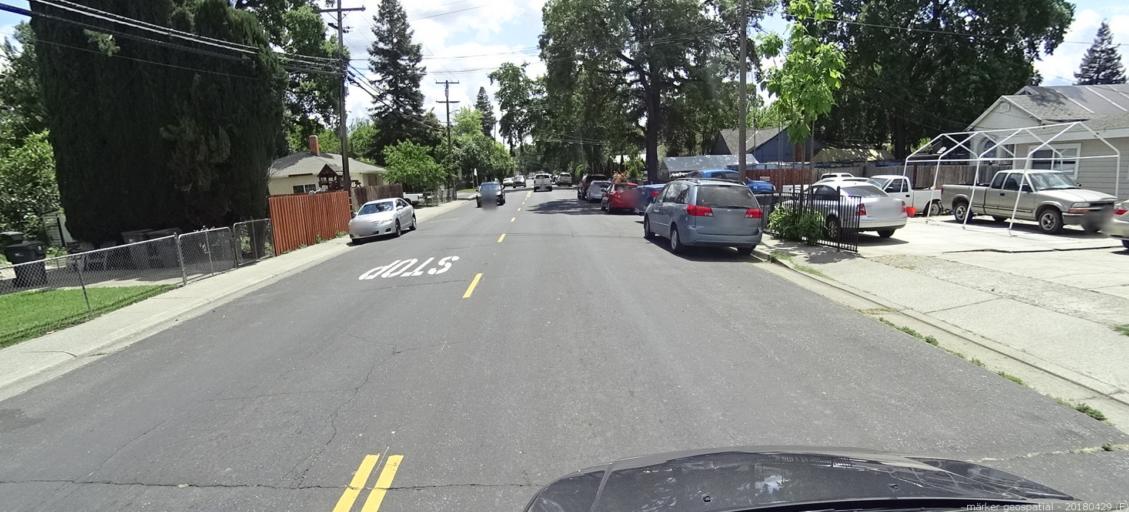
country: US
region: California
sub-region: Yolo County
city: West Sacramento
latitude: 38.5947
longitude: -121.5385
